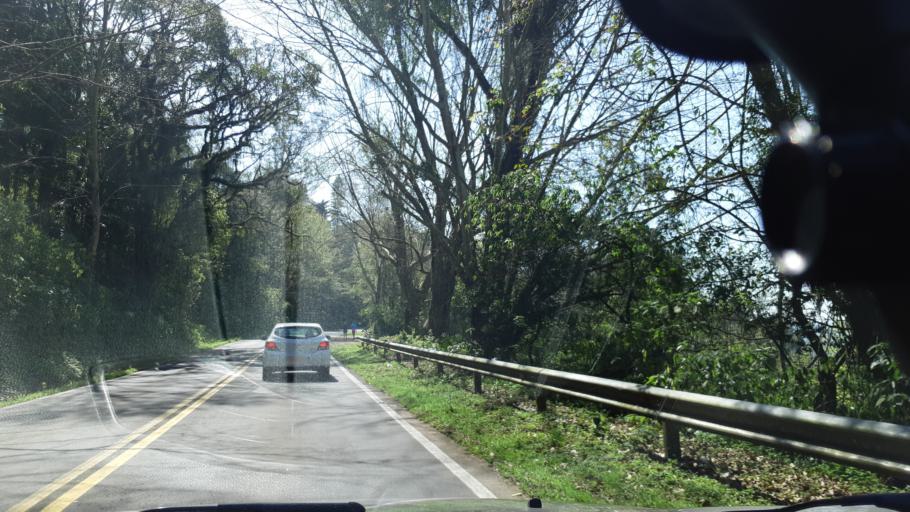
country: BR
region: Rio Grande do Sul
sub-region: Nova Petropolis
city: Nova Petropolis
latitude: -29.3974
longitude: -51.1272
